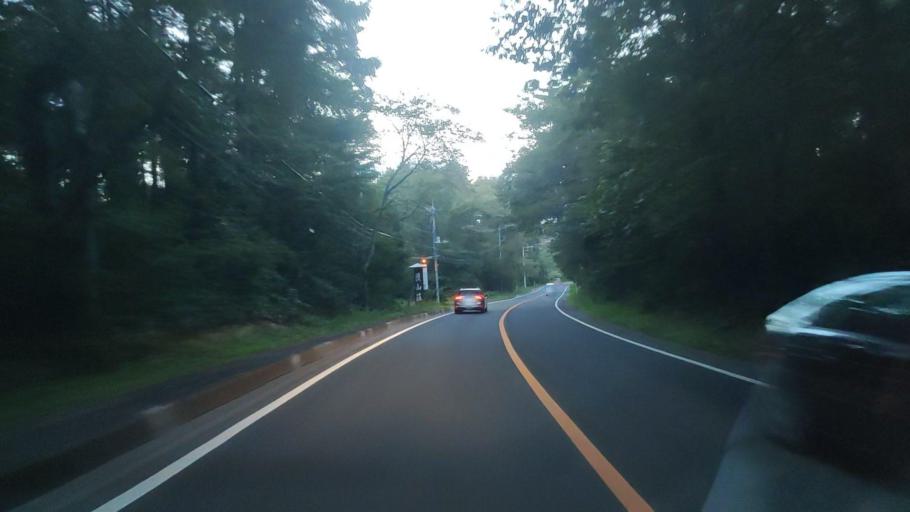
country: JP
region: Gunma
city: Nakanojomachi
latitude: 36.5190
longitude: 138.5981
